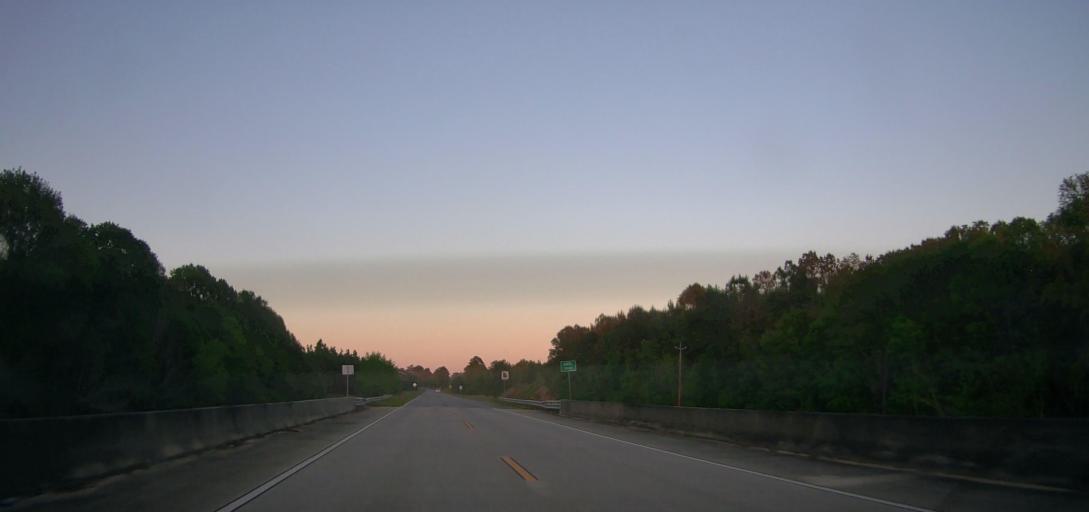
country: US
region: Georgia
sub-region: Wilcox County
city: Rochelle
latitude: 31.8158
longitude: -83.4743
